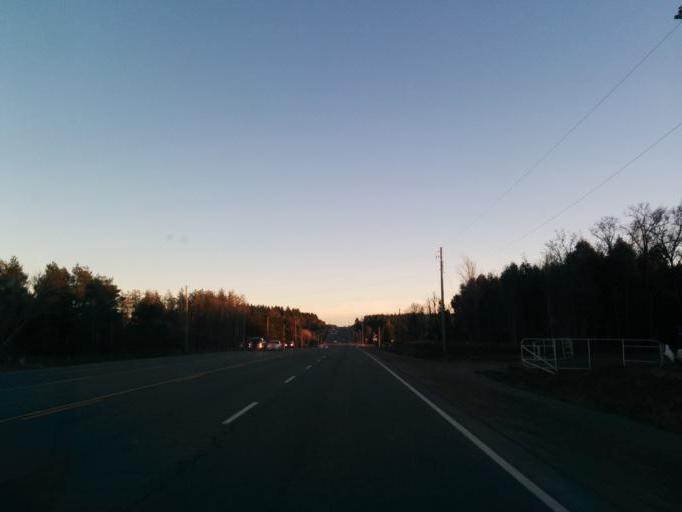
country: CA
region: Ontario
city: Orangeville
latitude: 43.9049
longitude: -80.0569
